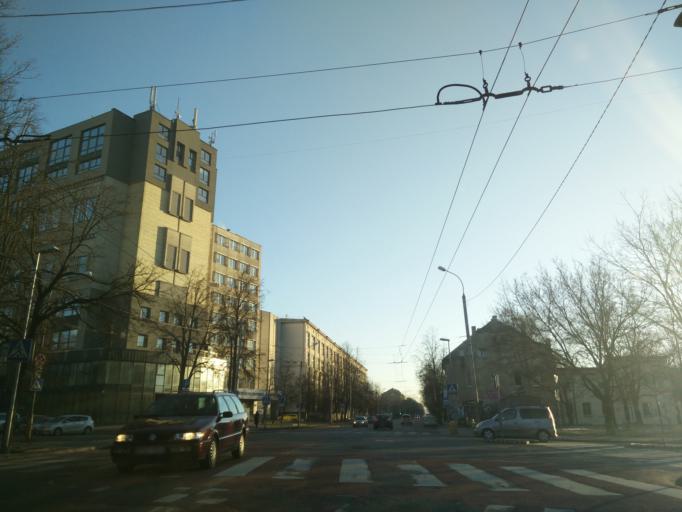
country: LT
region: Vilnius County
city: Naujamiestis
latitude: 54.6731
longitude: 25.2653
